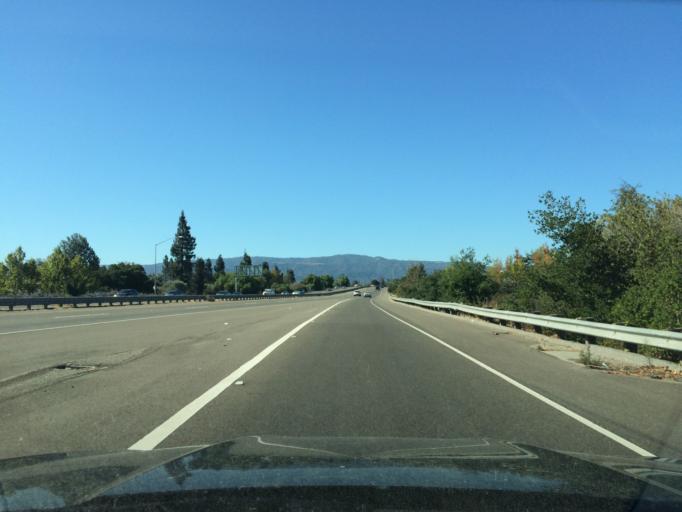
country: US
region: California
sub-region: Santa Clara County
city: Sunnyvale
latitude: 37.3912
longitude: -122.0525
